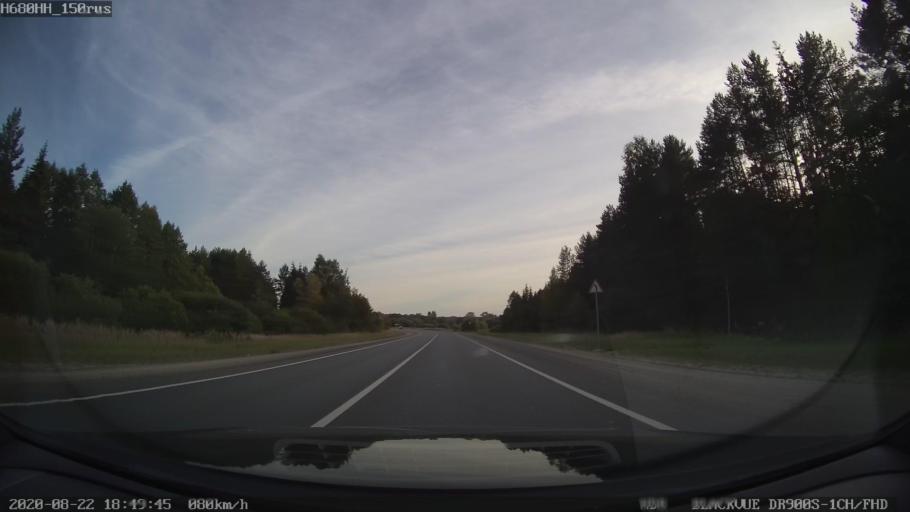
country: RU
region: Tverskaya
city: Rameshki
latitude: 57.2749
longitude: 36.0733
